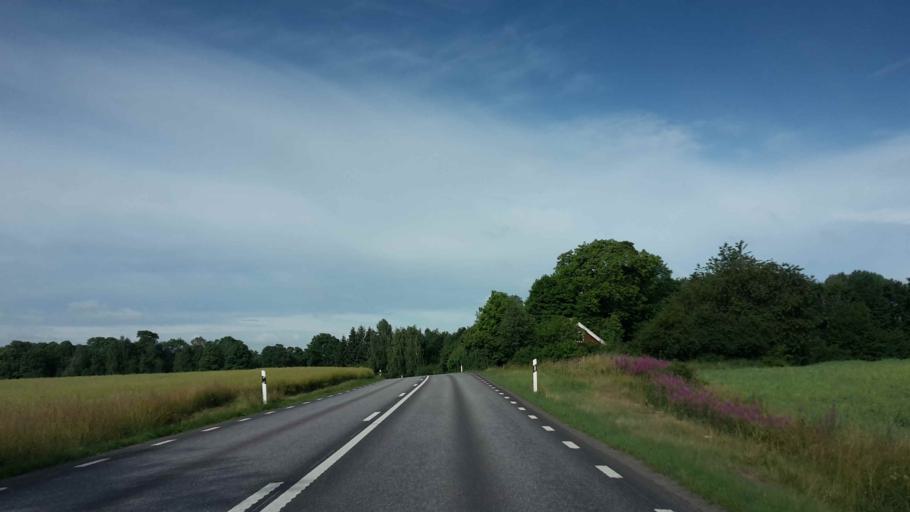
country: SE
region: OEstergoetland
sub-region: Motala Kommun
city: Borensberg
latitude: 58.5351
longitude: 15.3600
